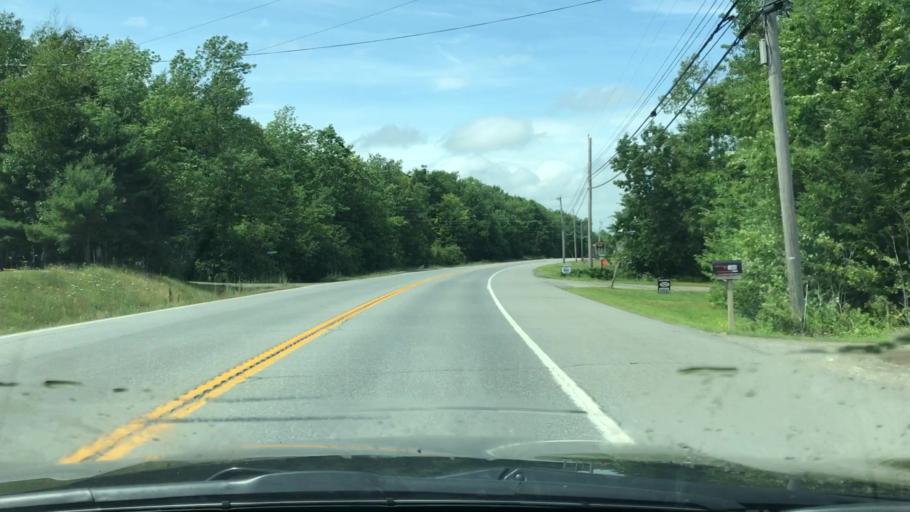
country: US
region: Maine
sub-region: Waldo County
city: Northport
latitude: 44.3594
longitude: -68.9737
